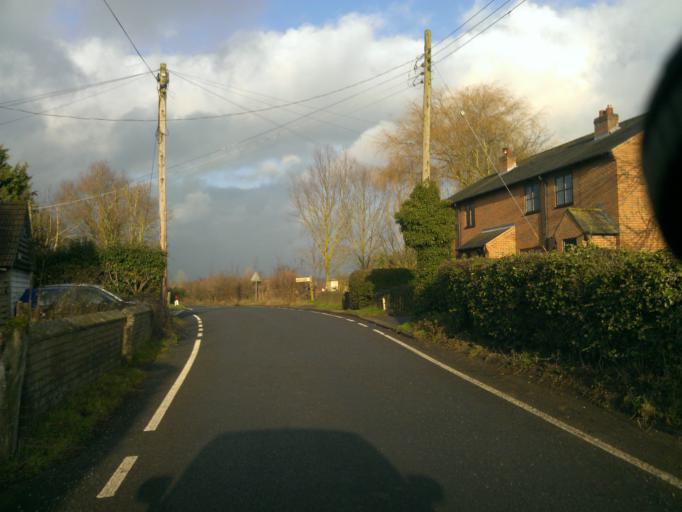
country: GB
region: England
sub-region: Suffolk
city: Sudbury
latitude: 52.0133
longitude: 0.7375
